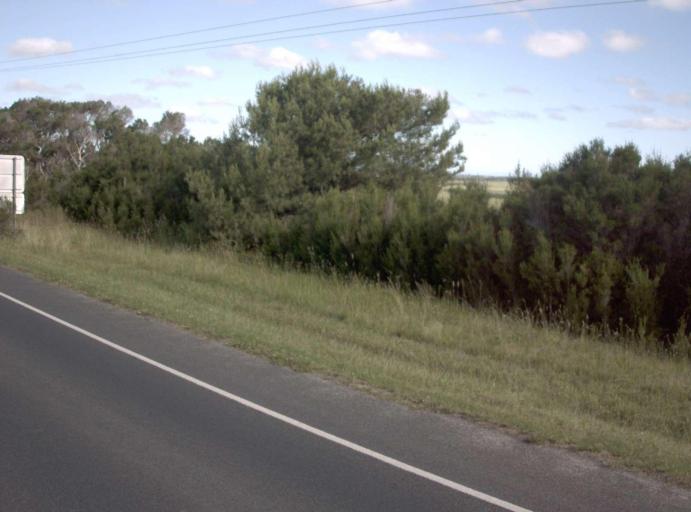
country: AU
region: Victoria
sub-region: Bass Coast
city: North Wonthaggi
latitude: -38.5638
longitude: 145.5502
